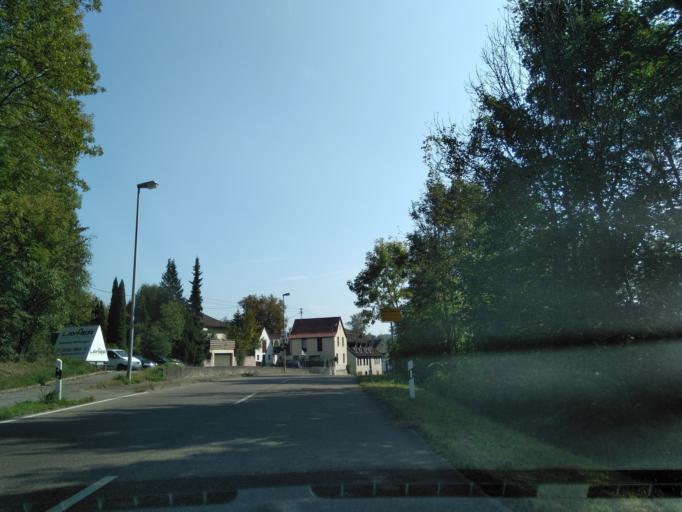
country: DE
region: Baden-Wuerttemberg
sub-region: Regierungsbezirk Stuttgart
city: Sersheim
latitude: 48.9639
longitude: 9.0524
